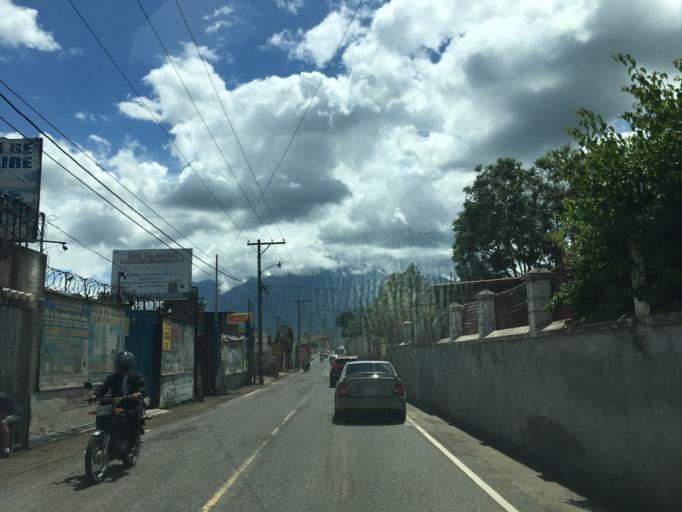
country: GT
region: Sacatepequez
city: Ciudad Vieja
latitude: 14.5269
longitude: -90.7608
